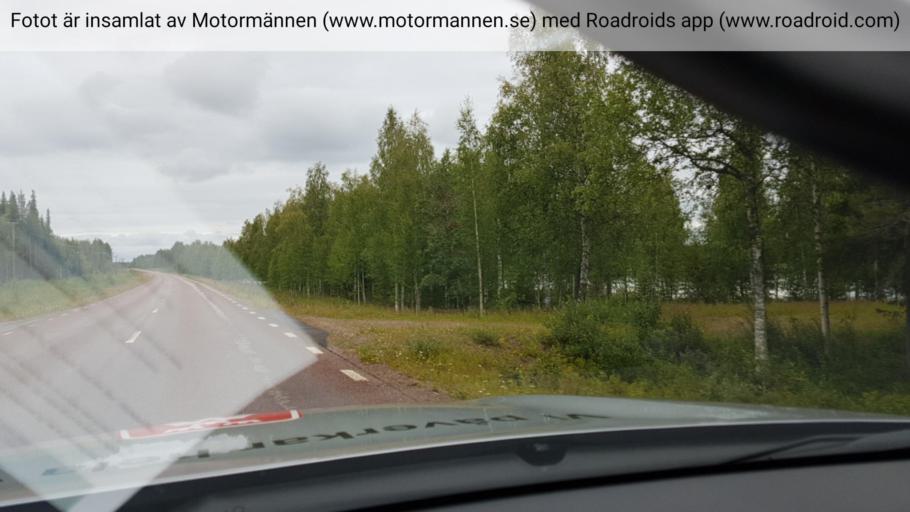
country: SE
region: Norrbotten
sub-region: Pajala Kommun
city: Pajala
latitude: 67.1154
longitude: 22.6039
